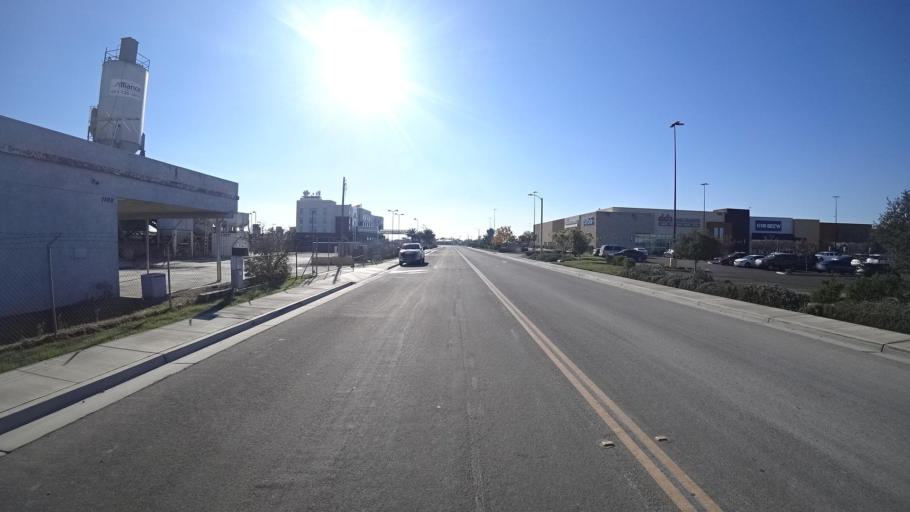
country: US
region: California
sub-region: Kern County
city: Delano
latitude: 35.7451
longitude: -119.2442
